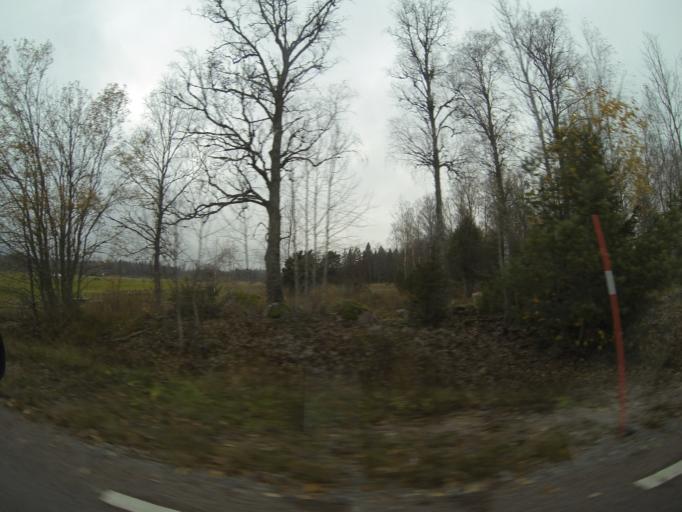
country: SE
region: Vaestmanland
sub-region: Surahammars Kommun
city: Ramnas
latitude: 59.7592
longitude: 16.1833
